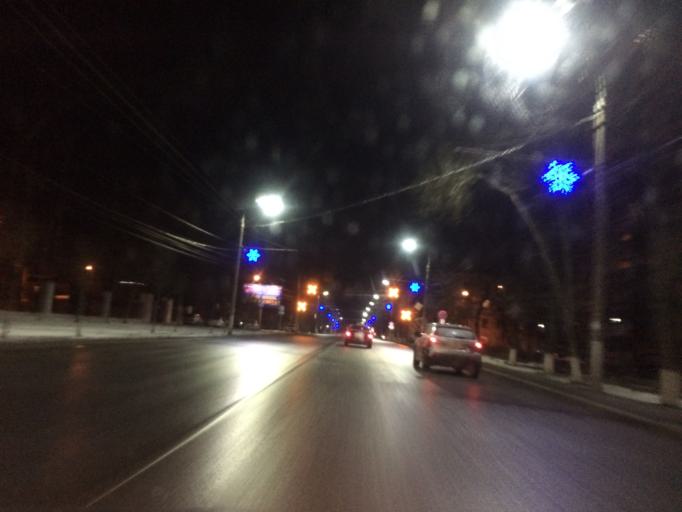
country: RU
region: Tula
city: Tula
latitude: 54.1876
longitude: 37.5879
